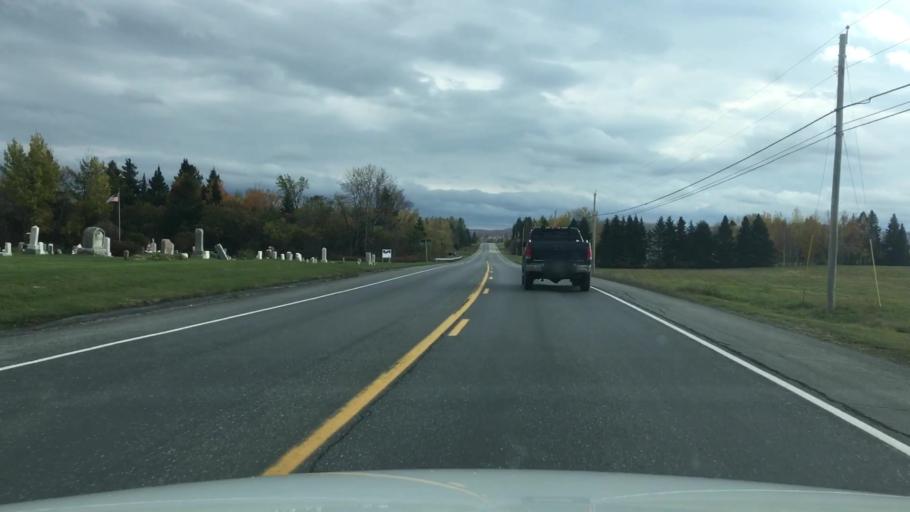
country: US
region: Maine
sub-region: Aroostook County
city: Easton
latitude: 46.5636
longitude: -67.9478
